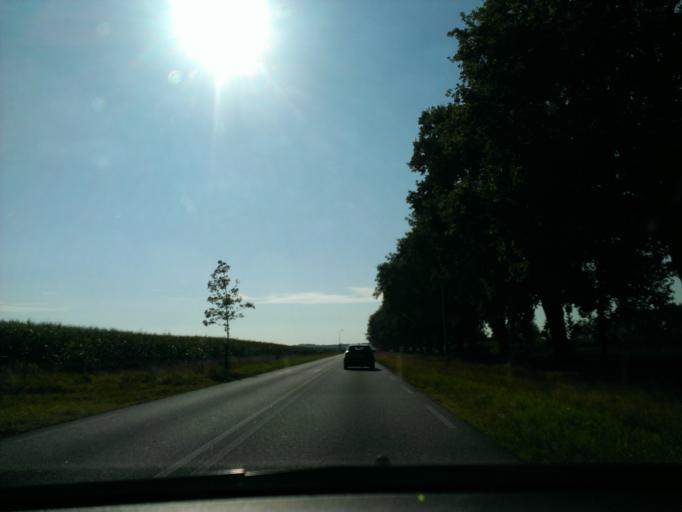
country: NL
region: Drenthe
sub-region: Gemeente Coevorden
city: Dalen
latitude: 52.7221
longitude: 6.7349
